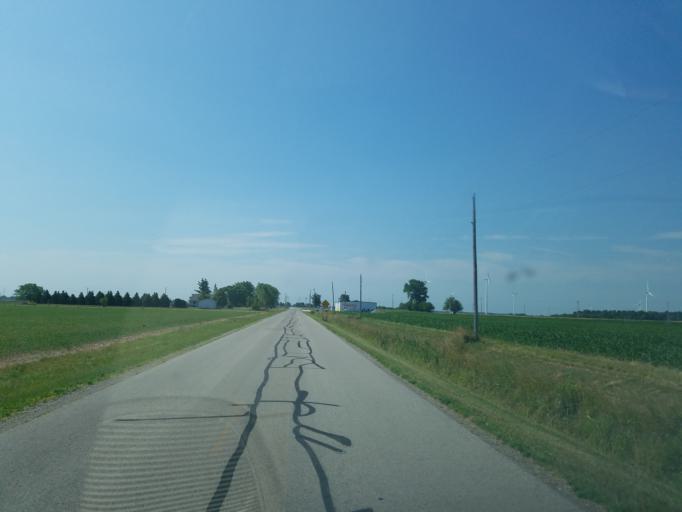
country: US
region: Ohio
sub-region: Van Wert County
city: Convoy
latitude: 40.9485
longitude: -84.6299
